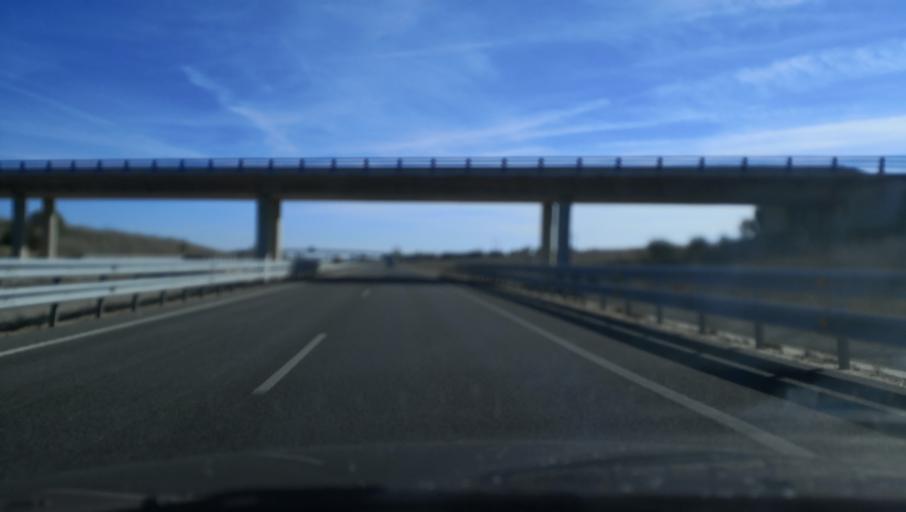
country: ES
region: Castille and Leon
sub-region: Provincia de Salamanca
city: Villar de Gallimazo
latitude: 40.9276
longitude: -5.3037
